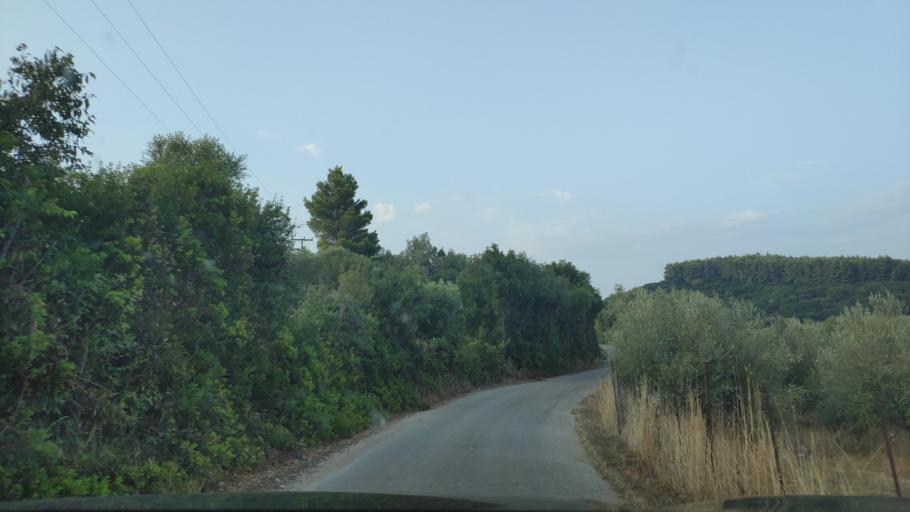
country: GR
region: West Greece
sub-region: Nomos Aitolias kai Akarnanias
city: Monastirakion
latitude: 38.9156
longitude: 20.9662
